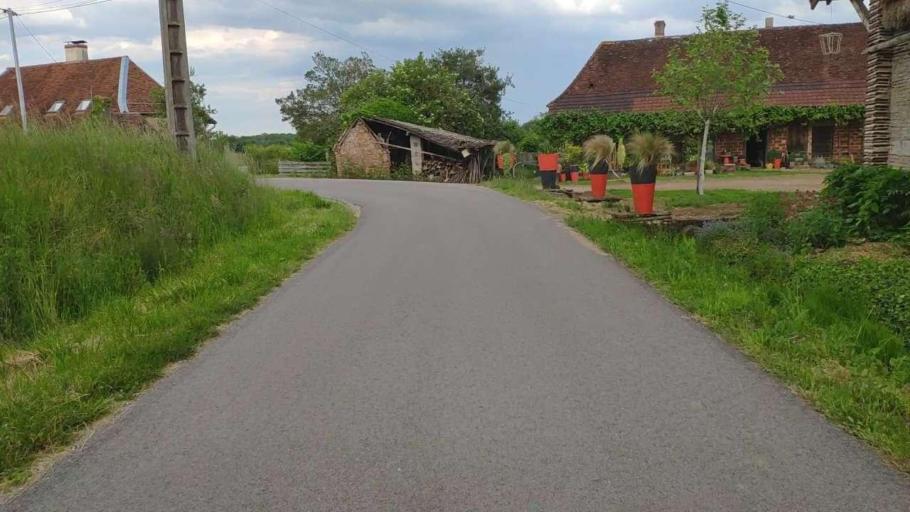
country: FR
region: Franche-Comte
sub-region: Departement du Jura
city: Bletterans
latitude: 46.7964
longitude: 5.3658
